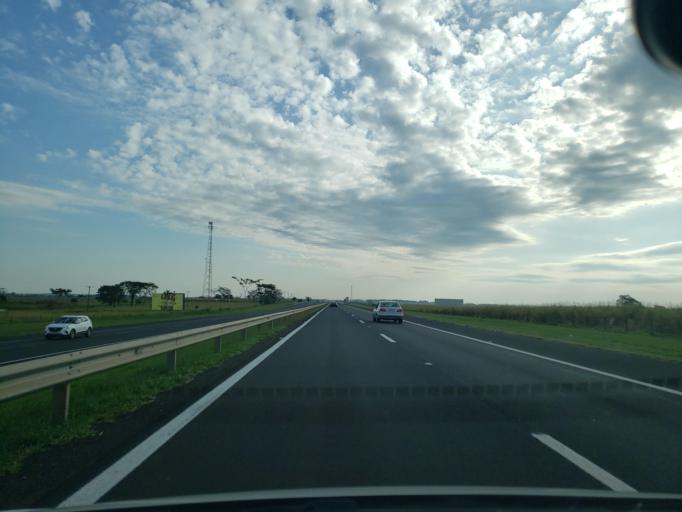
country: BR
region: Sao Paulo
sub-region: Guararapes
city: Guararapes
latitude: -21.2057
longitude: -50.6308
